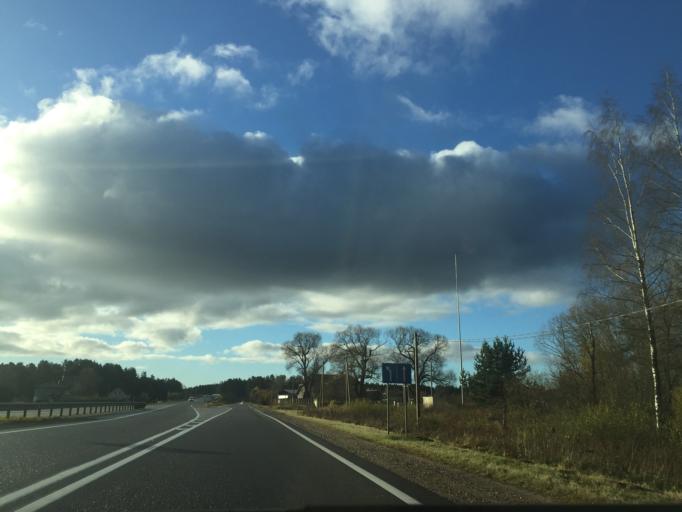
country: LV
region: Babite
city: Pinki
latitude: 56.9290
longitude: 23.9159
